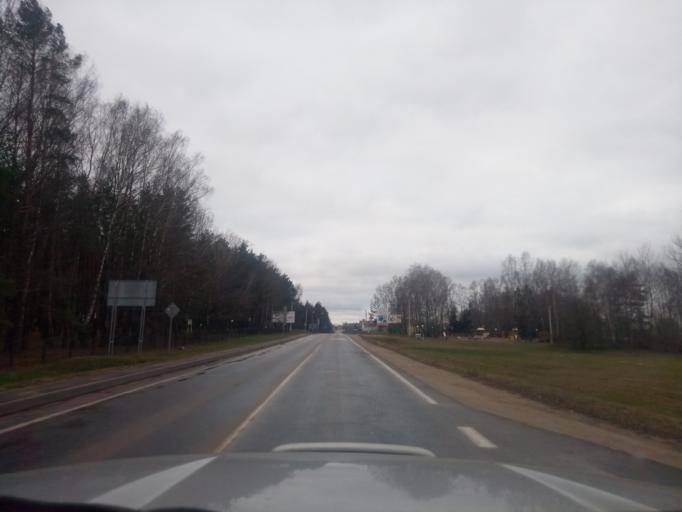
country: BY
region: Minsk
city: Kapyl'
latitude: 53.1565
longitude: 27.1029
